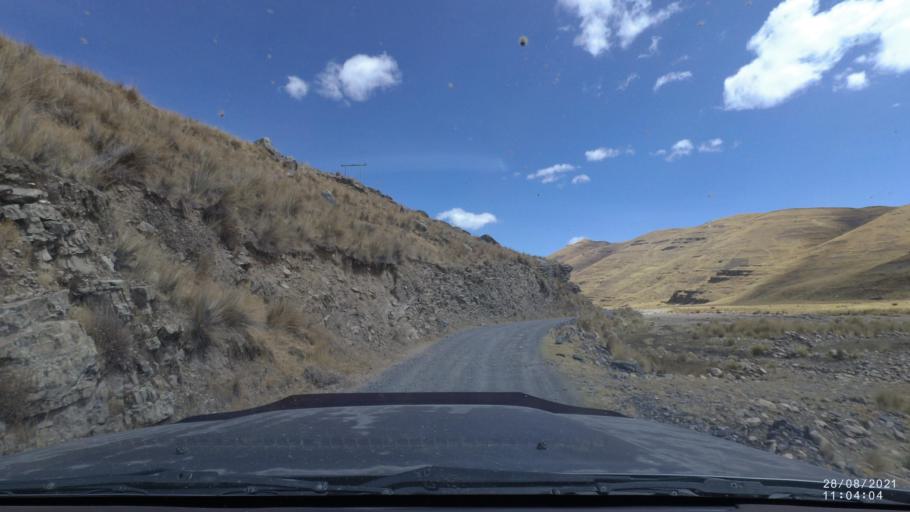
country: BO
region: Cochabamba
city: Cochabamba
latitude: -17.1752
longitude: -66.2806
